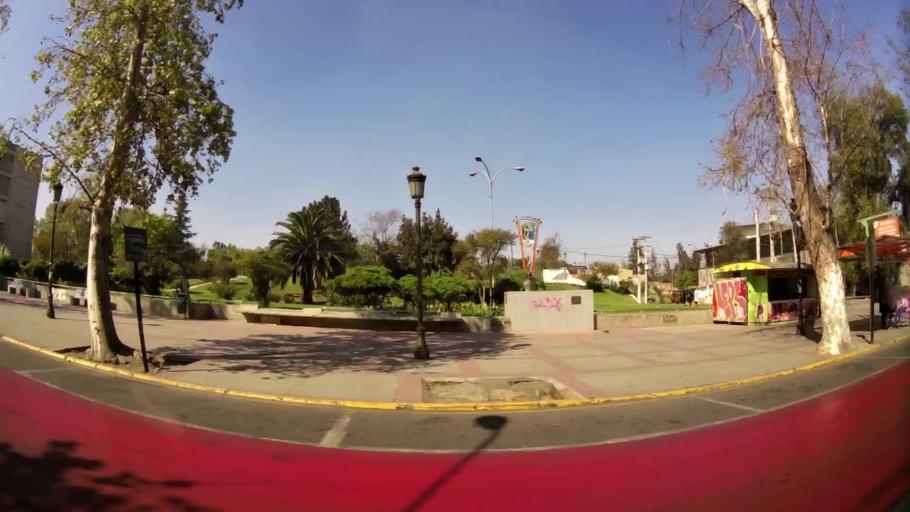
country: CL
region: Santiago Metropolitan
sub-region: Provincia de Santiago
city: Lo Prado
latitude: -33.5082
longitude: -70.7572
